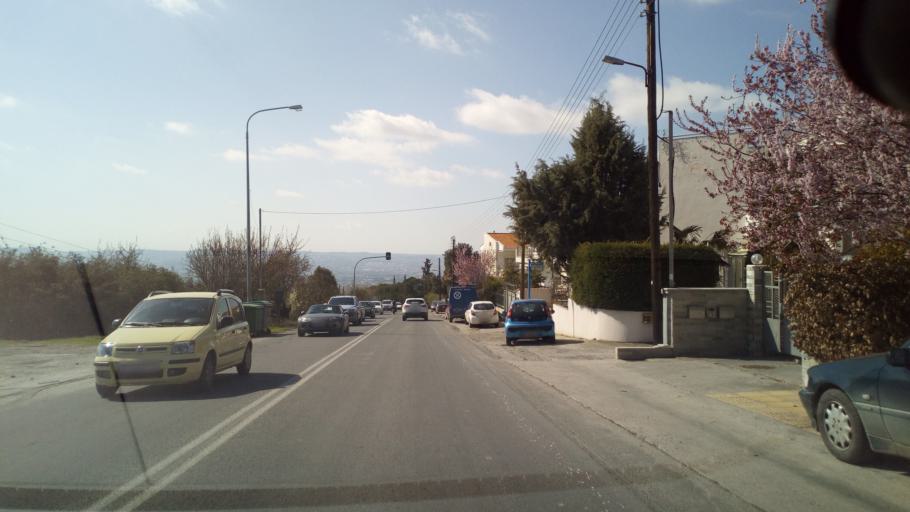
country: GR
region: Central Macedonia
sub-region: Nomos Thessalonikis
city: Panorama
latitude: 40.5753
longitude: 23.0260
